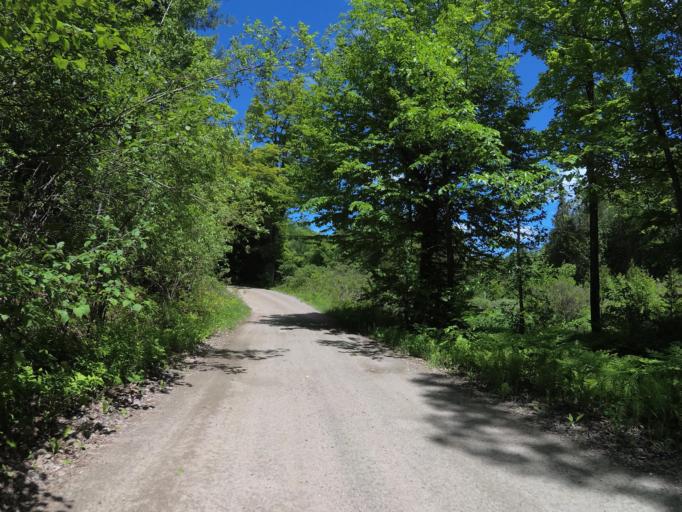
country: CA
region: Ontario
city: Renfrew
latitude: 45.0099
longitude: -76.8990
